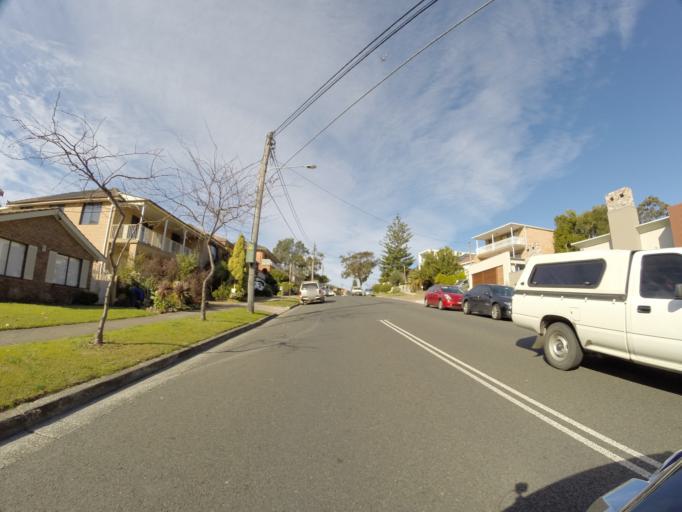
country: AU
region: New South Wales
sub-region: Randwick
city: South Coogee
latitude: -33.9388
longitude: 151.2483
